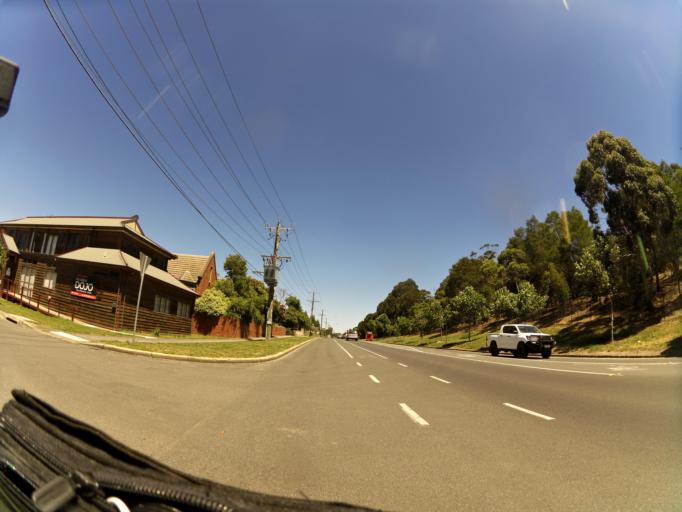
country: AU
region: Victoria
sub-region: Ballarat North
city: Golden Point
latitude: -37.5778
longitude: 143.8682
